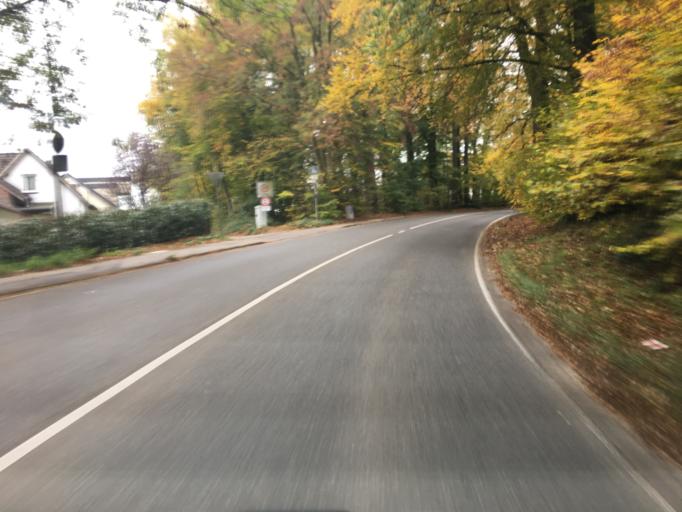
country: DE
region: North Rhine-Westphalia
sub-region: Regierungsbezirk Dusseldorf
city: Heiligenhaus
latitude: 51.3189
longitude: 6.9558
